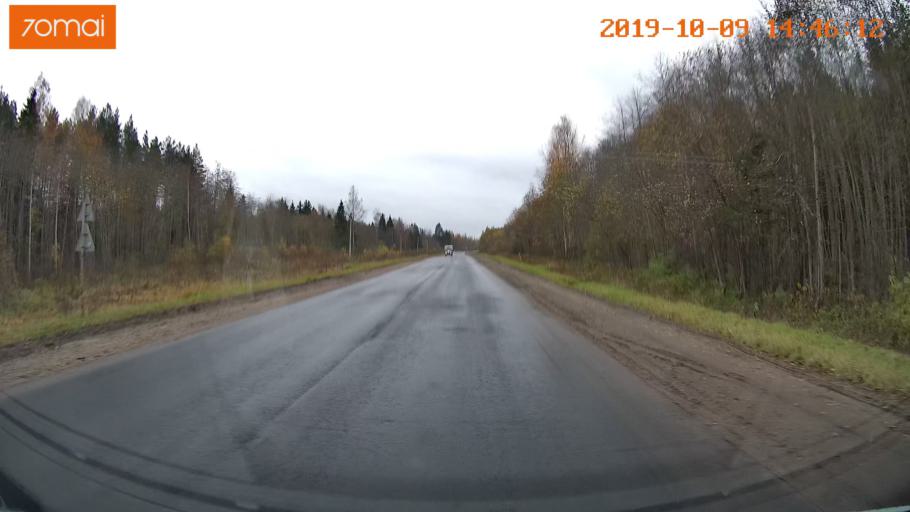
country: RU
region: Kostroma
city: Buy
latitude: 58.4345
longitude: 41.5771
